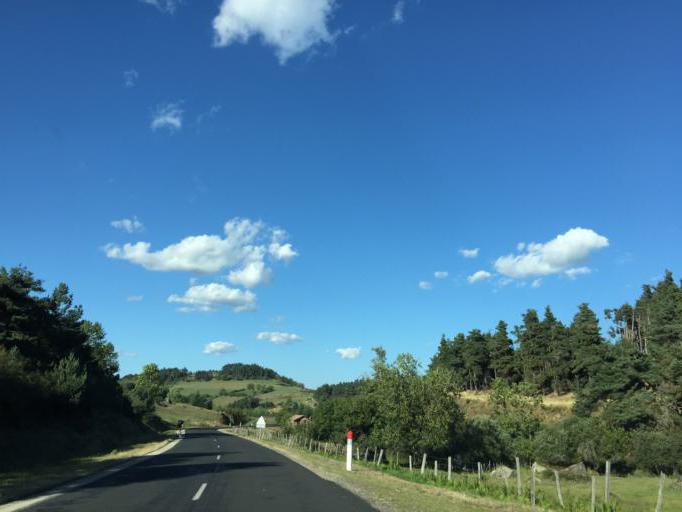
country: FR
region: Auvergne
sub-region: Departement de la Haute-Loire
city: Saugues
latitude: 44.9657
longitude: 3.6083
